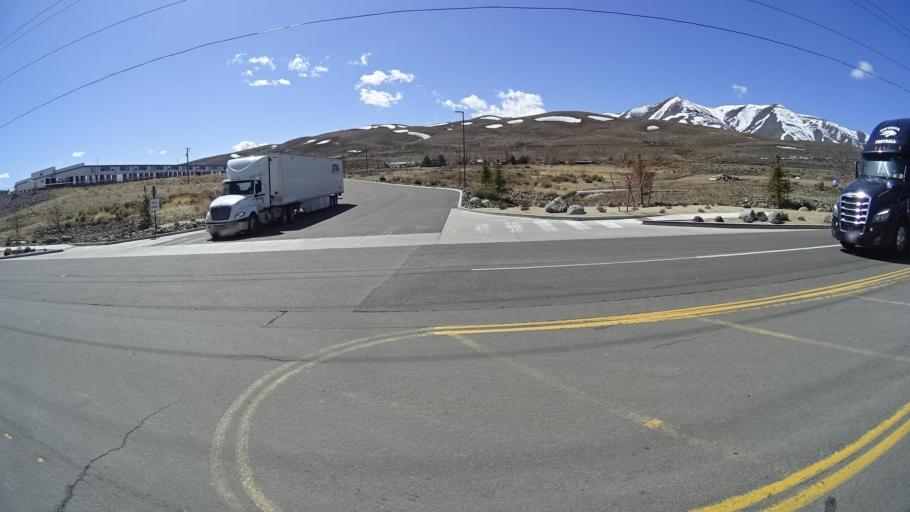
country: US
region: Nevada
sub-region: Washoe County
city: Lemmon Valley
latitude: 39.6163
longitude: -119.8752
